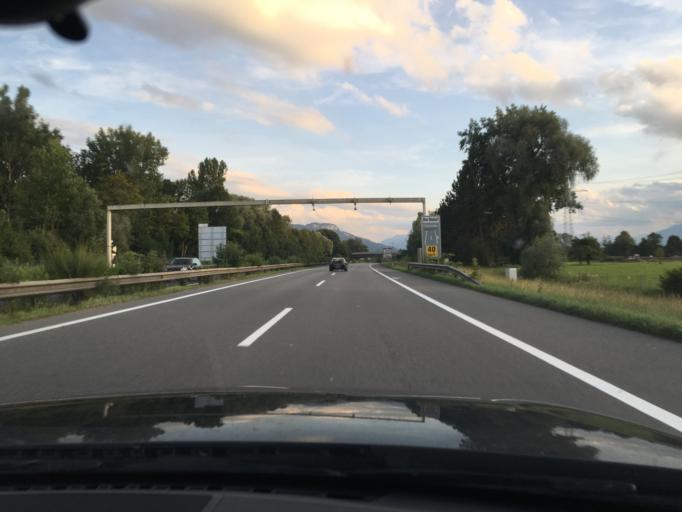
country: AT
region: Vorarlberg
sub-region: Politischer Bezirk Dornbirn
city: Dornbirn
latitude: 47.4322
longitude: 9.7203
